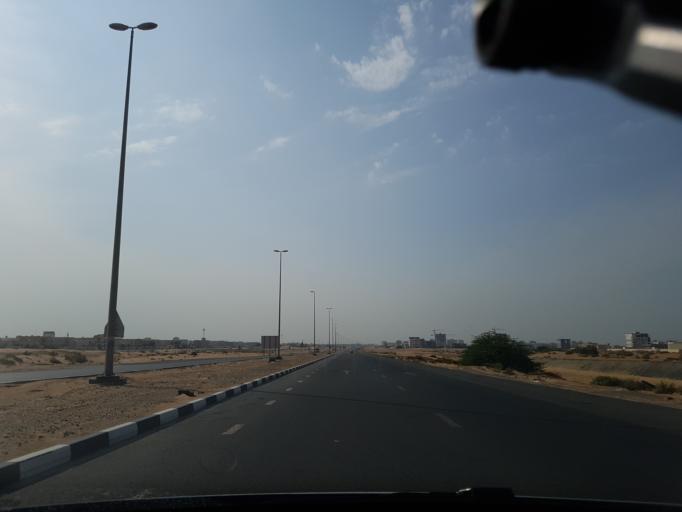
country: AE
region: Ajman
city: Ajman
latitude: 25.4142
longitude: 55.5555
